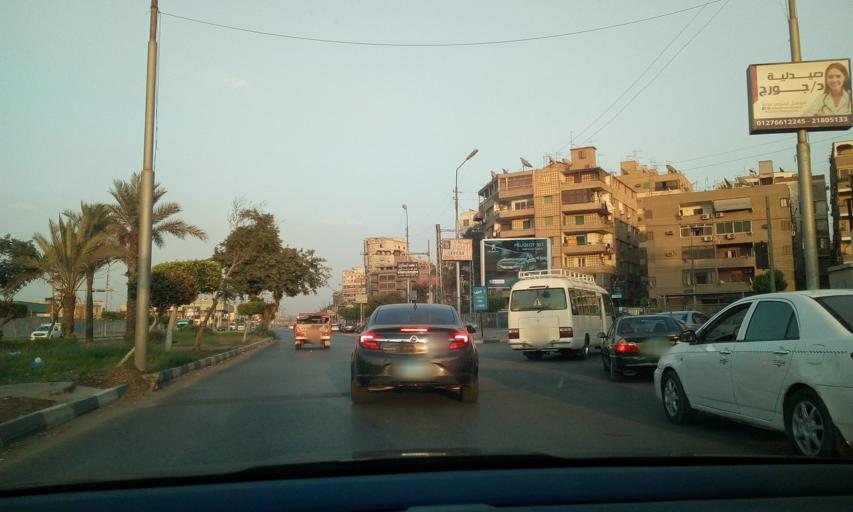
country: EG
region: Muhafazat al Qalyubiyah
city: Al Khankah
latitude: 30.1187
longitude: 31.3556
